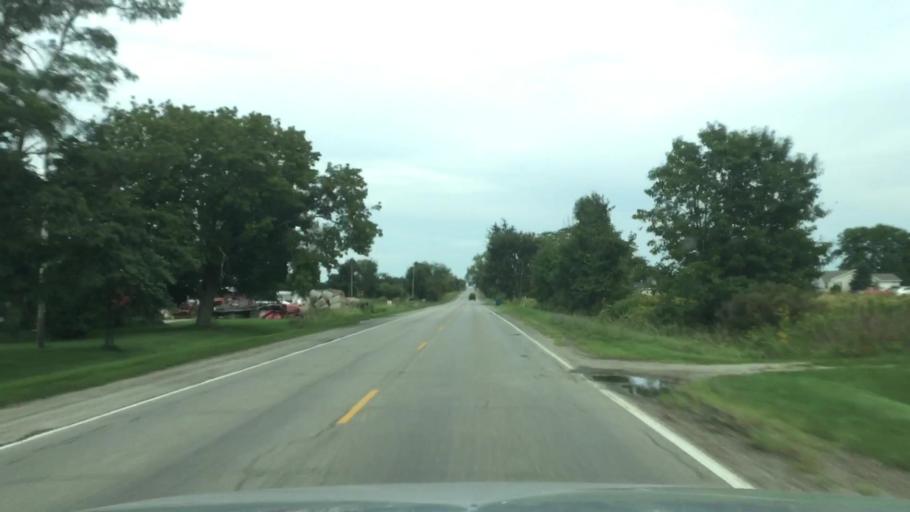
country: US
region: Michigan
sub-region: Genesee County
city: Lake Fenton
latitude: 42.8850
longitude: -83.7524
